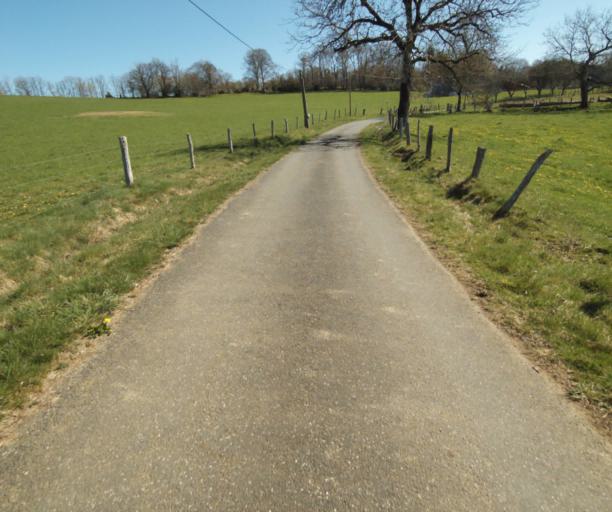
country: FR
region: Limousin
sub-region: Departement de la Correze
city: Chamboulive
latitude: 45.4222
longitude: 1.7368
